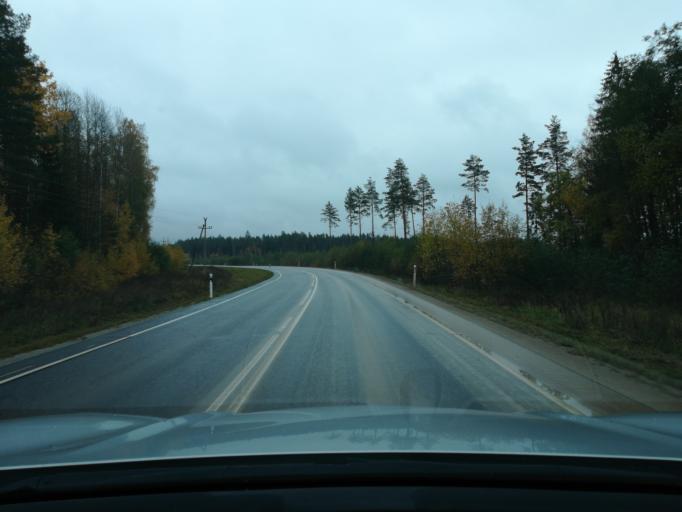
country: EE
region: Ida-Virumaa
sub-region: Johvi vald
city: Johvi
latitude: 59.3011
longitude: 27.4696
